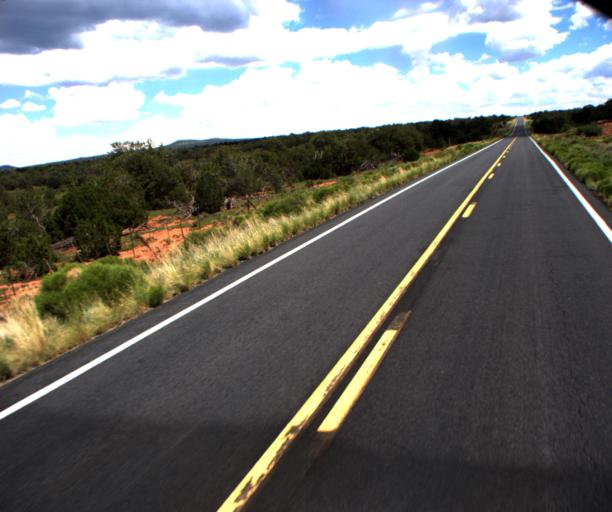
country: US
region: Arizona
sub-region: Coconino County
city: Parks
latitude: 35.6025
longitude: -112.0333
